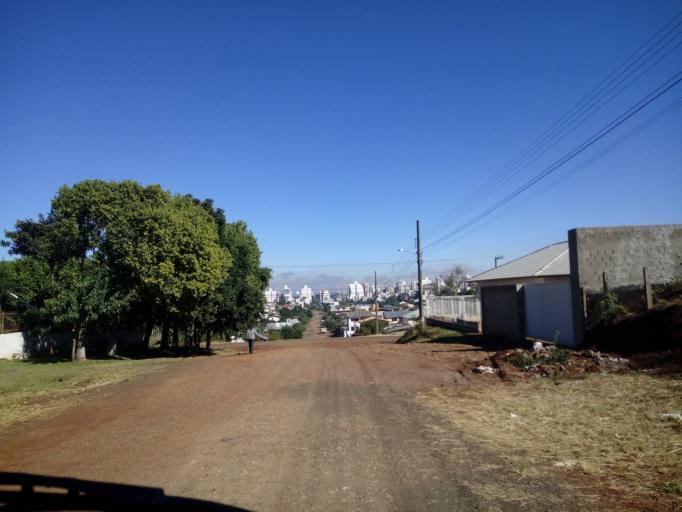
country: BR
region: Santa Catarina
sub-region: Chapeco
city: Chapeco
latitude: -27.0948
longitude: -52.5963
